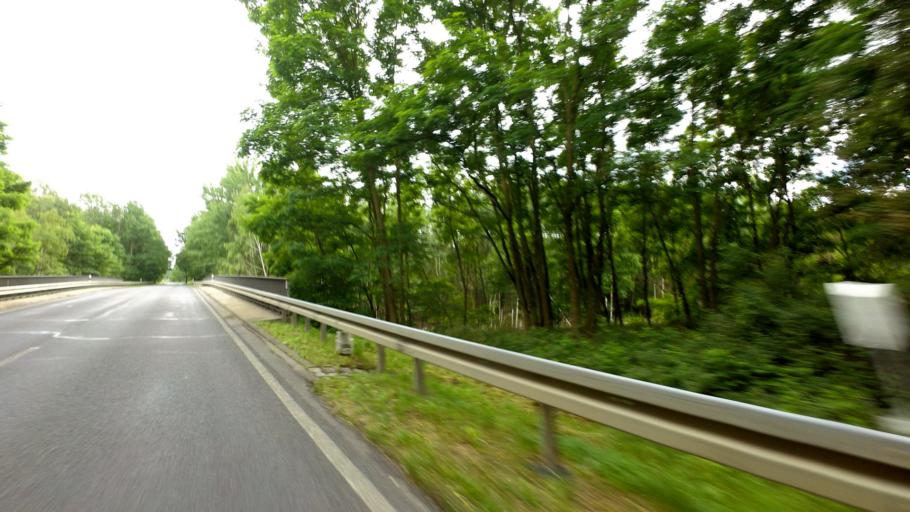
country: DE
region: Brandenburg
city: Calau
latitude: 51.7912
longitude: 13.8655
